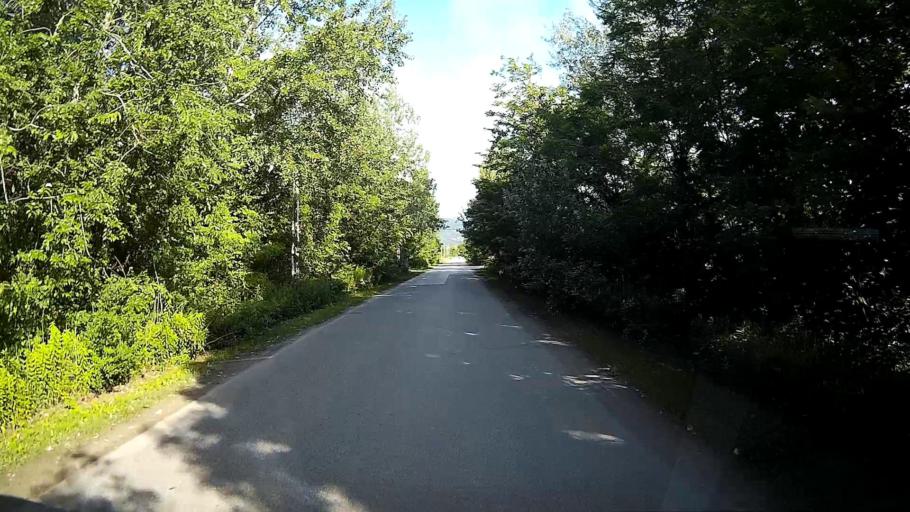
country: HU
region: Pest
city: God
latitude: 47.6806
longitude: 19.1121
